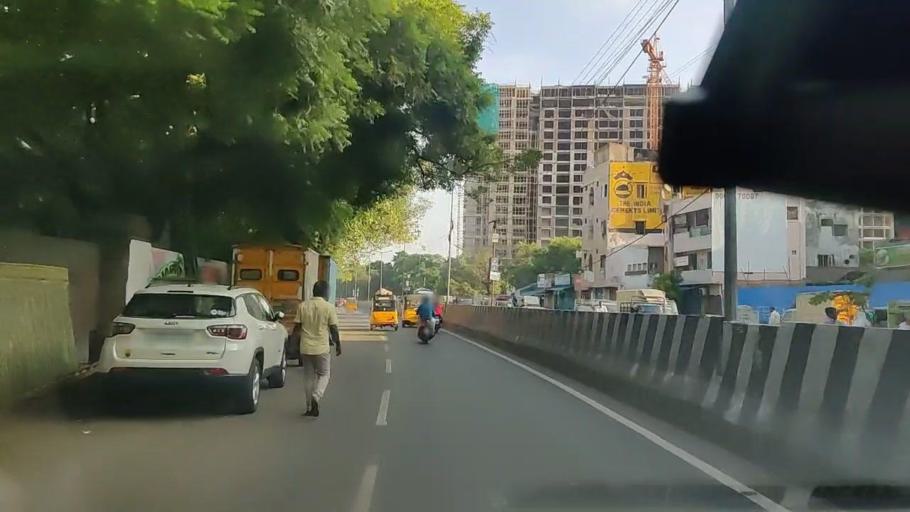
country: IN
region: Tamil Nadu
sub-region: Chennai
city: George Town
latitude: 13.0999
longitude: 80.2751
